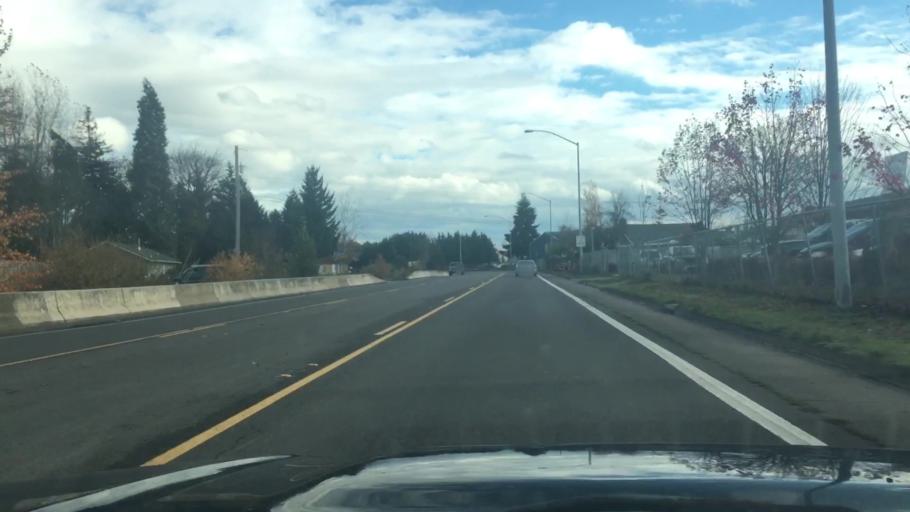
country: US
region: Oregon
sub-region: Lane County
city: Eugene
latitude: 44.0641
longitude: -123.1597
